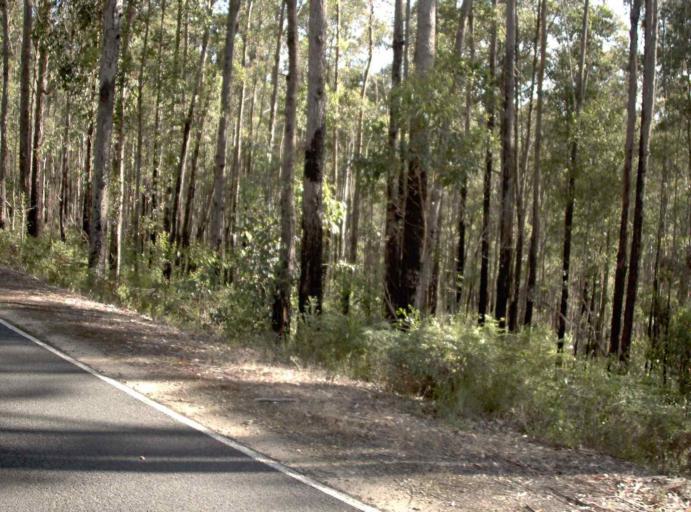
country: AU
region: Victoria
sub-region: East Gippsland
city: Lakes Entrance
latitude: -37.6641
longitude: 148.4777
